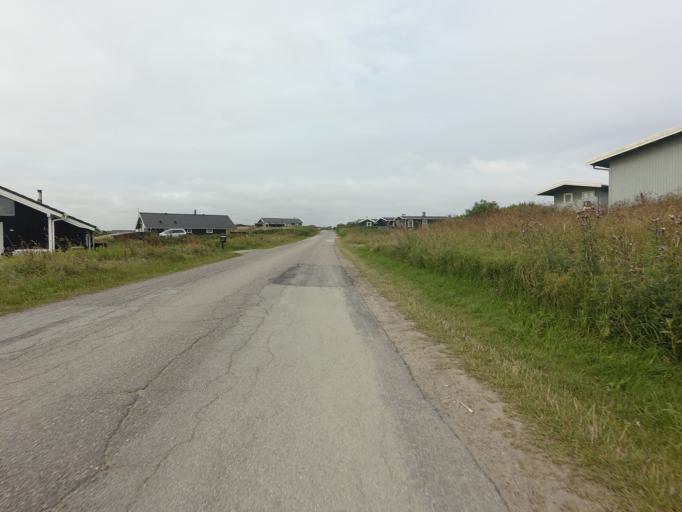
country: DK
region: North Denmark
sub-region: Jammerbugt Kommune
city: Pandrup
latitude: 57.3876
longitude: 9.7274
